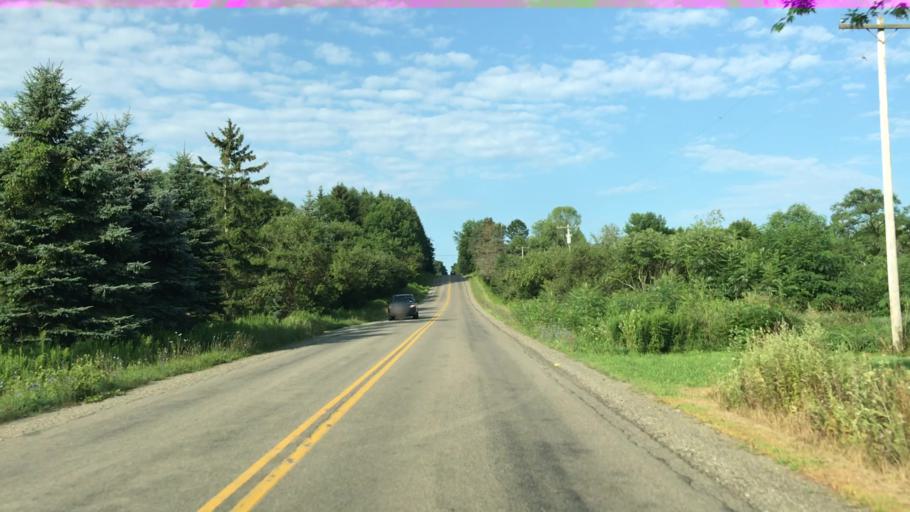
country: US
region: New York
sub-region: Chautauqua County
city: Brocton
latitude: 42.3098
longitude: -79.3758
